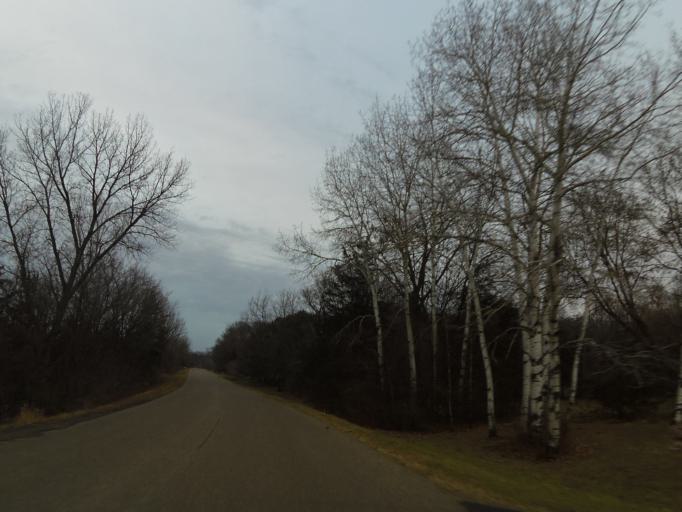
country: US
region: Wisconsin
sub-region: Pierce County
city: River Falls
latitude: 44.8782
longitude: -92.6131
